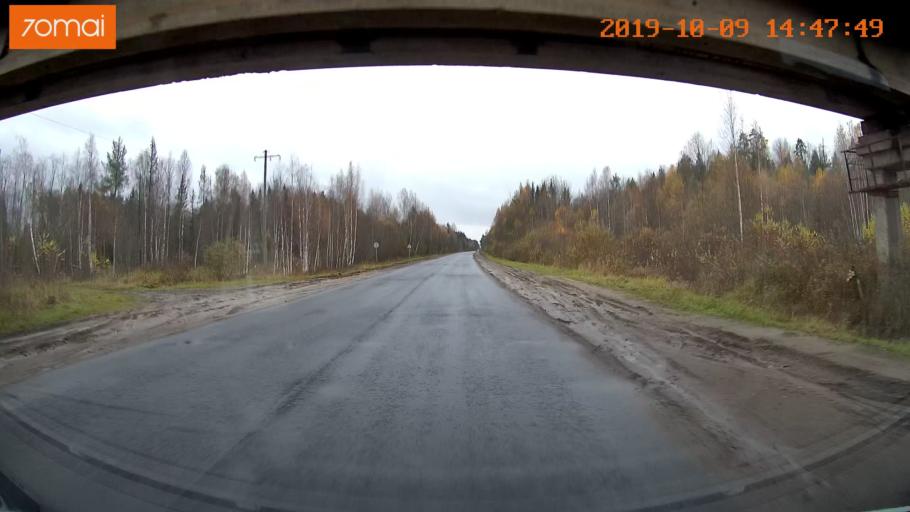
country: RU
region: Kostroma
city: Chistyye Bory
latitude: 58.4136
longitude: 41.5722
